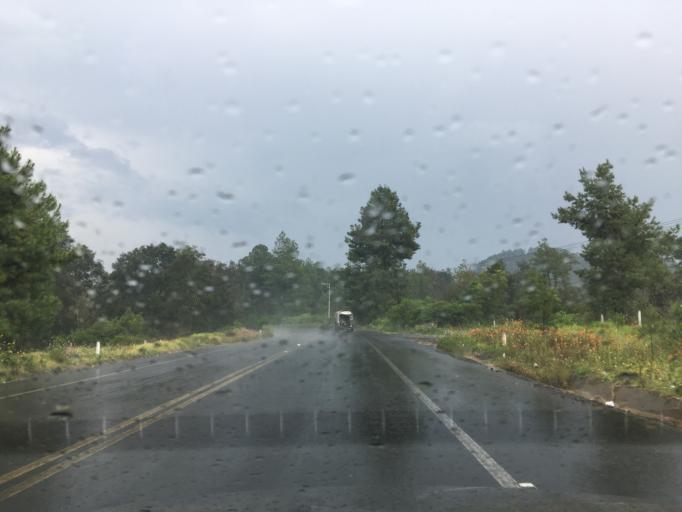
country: MX
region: Michoacan
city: Angahuan
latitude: 19.5674
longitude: -102.2777
